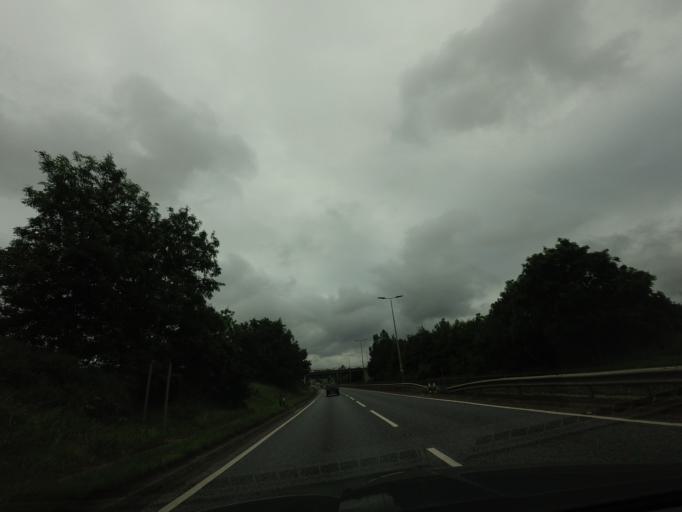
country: GB
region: Scotland
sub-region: Highland
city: Inverness
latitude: 57.4733
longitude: -4.1856
